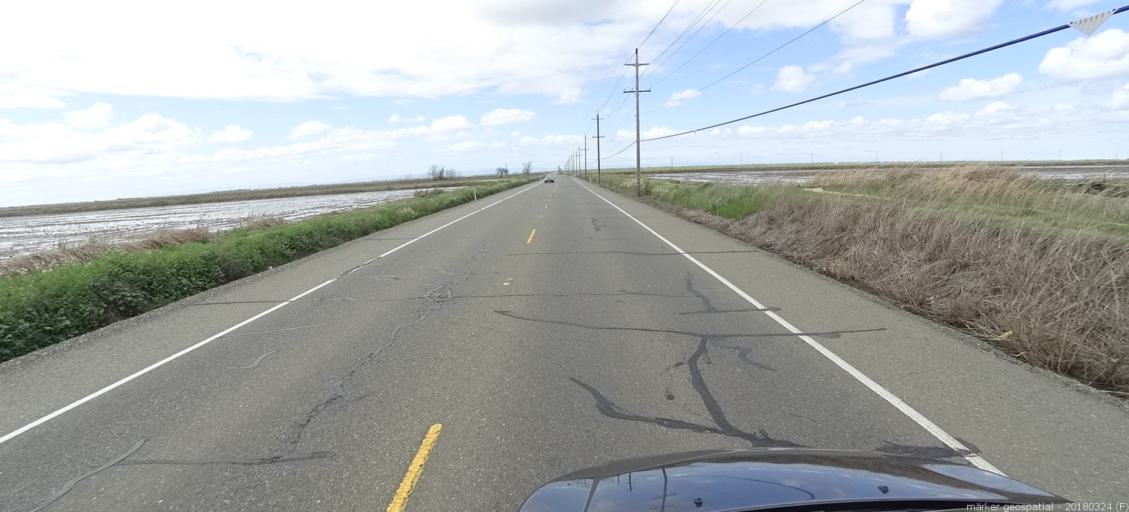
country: US
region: California
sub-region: Sacramento County
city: Elverta
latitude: 38.7145
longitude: -121.4978
